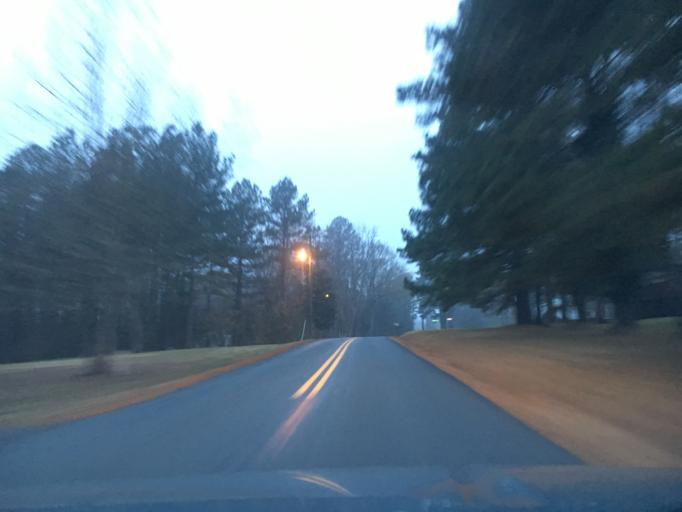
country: US
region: Virginia
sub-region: Halifax County
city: Mountain Road
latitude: 36.6833
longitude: -79.0125
